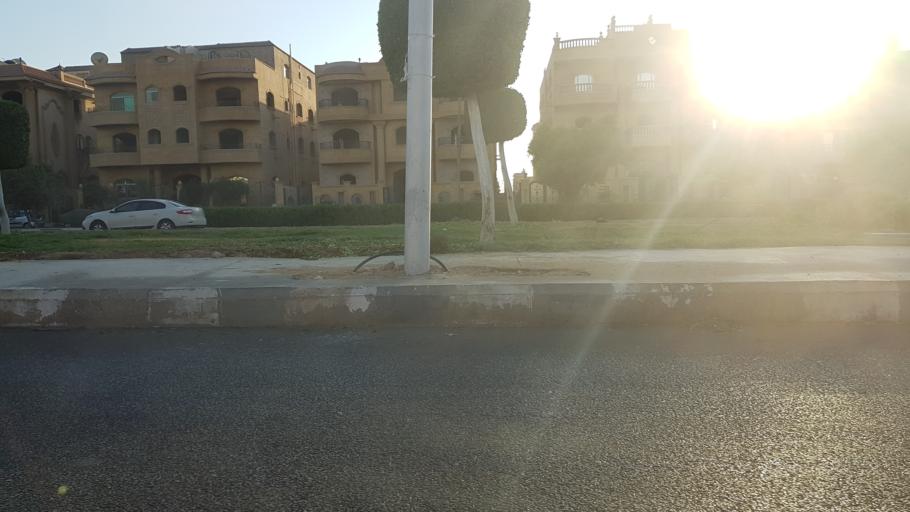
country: EG
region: Muhafazat al Qalyubiyah
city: Al Khankah
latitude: 30.0346
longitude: 31.4396
